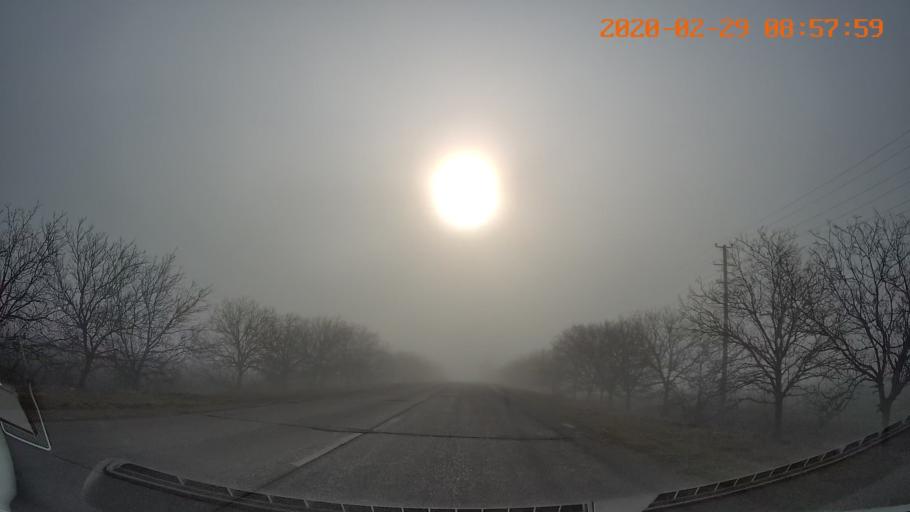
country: MD
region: Telenesti
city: Tiraspolul Nou
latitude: 46.9242
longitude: 29.6344
